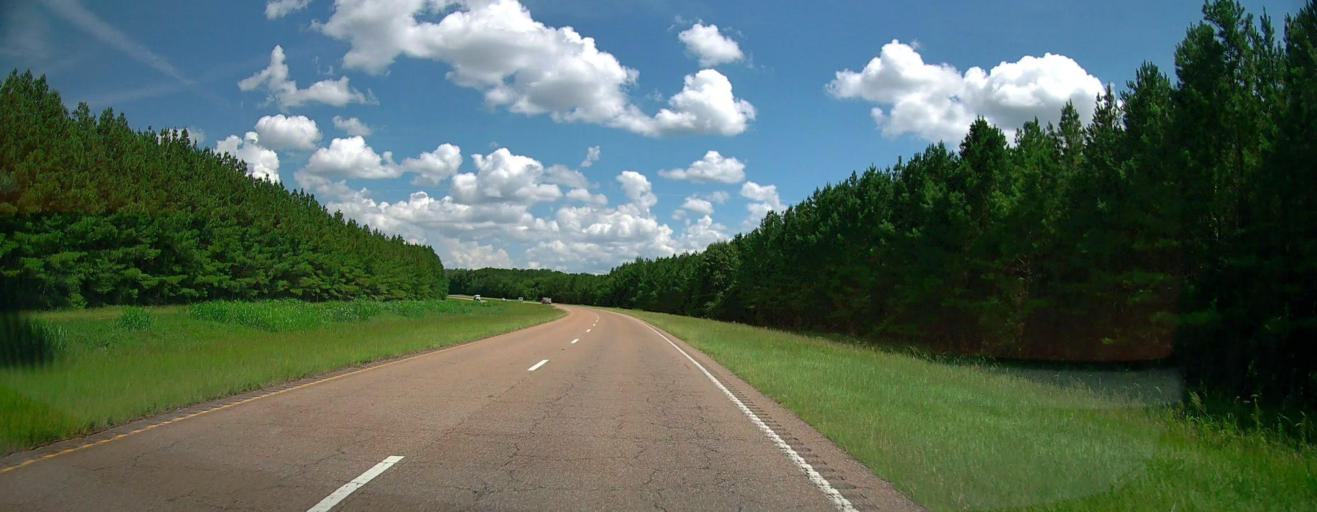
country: US
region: Mississippi
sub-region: Monroe County
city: Aberdeen
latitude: 33.8208
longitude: -88.5824
